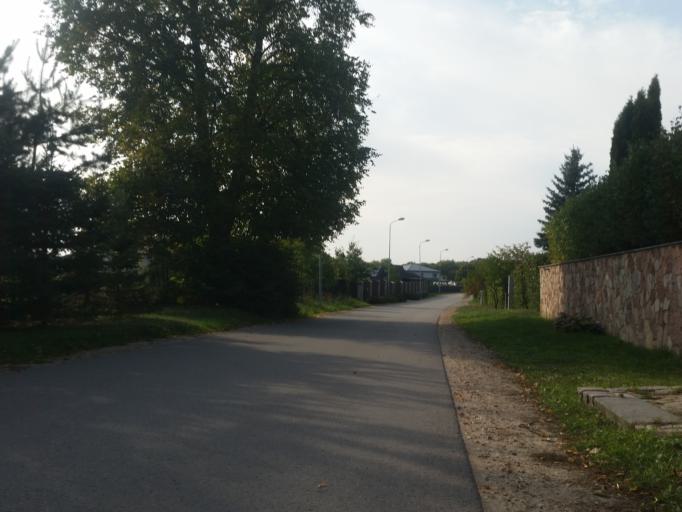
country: LV
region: Ikskile
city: Ikskile
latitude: 56.8201
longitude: 24.5062
